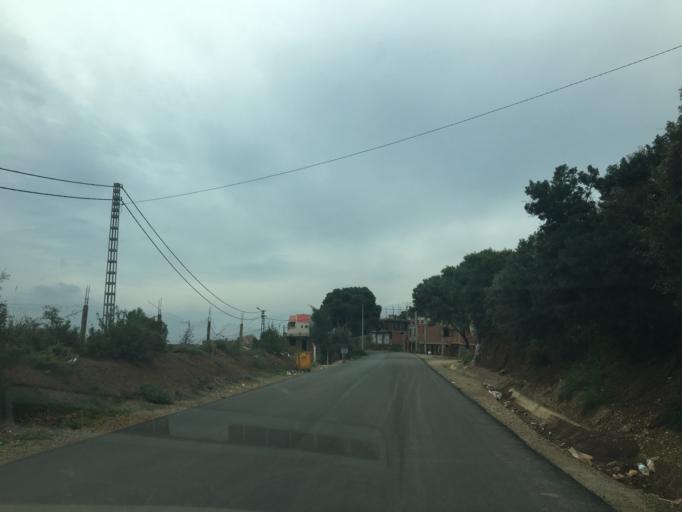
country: DZ
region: Tipaza
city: Tipasa
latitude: 36.6365
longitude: 2.3155
